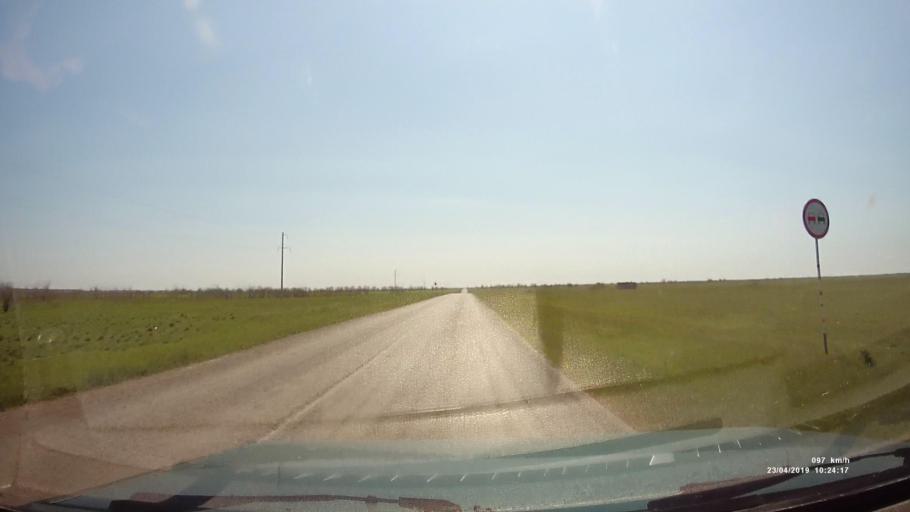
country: RU
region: Rostov
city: Sovetskoye
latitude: 46.6402
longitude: 42.4391
